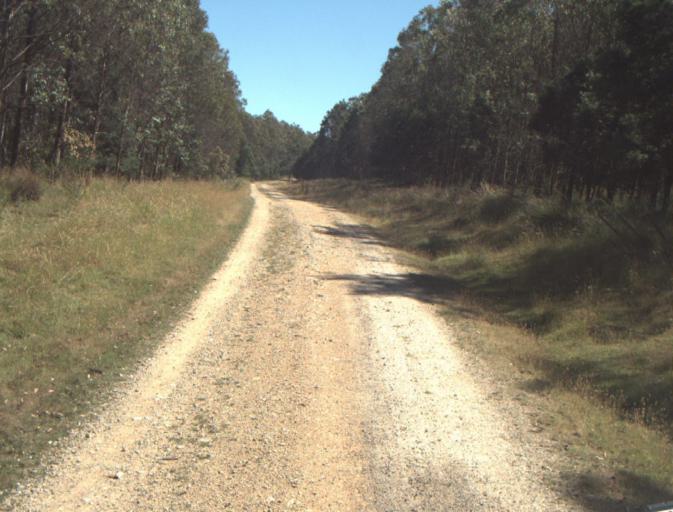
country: AU
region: Tasmania
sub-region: Dorset
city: Scottsdale
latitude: -41.2676
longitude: 147.3517
